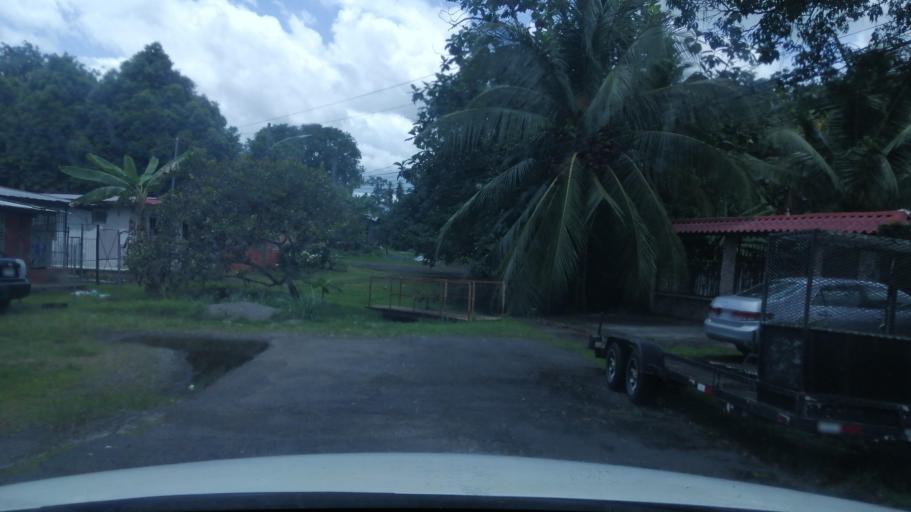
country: PA
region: Chiriqui
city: David
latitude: 8.4238
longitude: -82.4407
